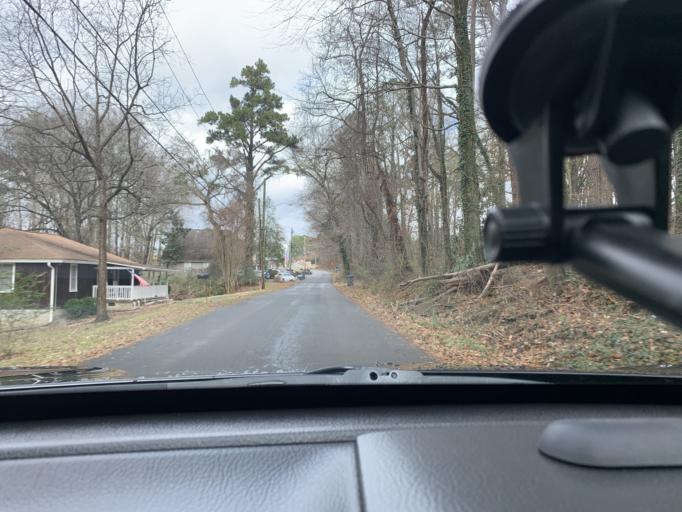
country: US
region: Georgia
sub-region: Cobb County
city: Acworth
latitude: 34.0723
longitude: -84.6755
